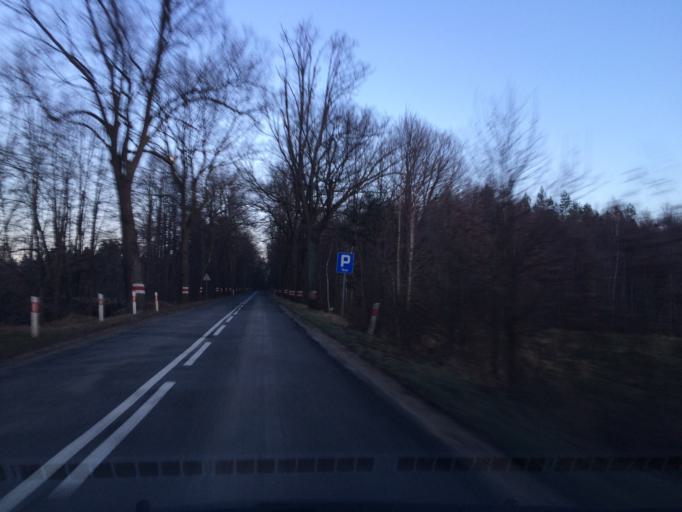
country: PL
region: Lower Silesian Voivodeship
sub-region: Powiat lwowecki
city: Wlen
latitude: 51.1195
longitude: 15.7063
